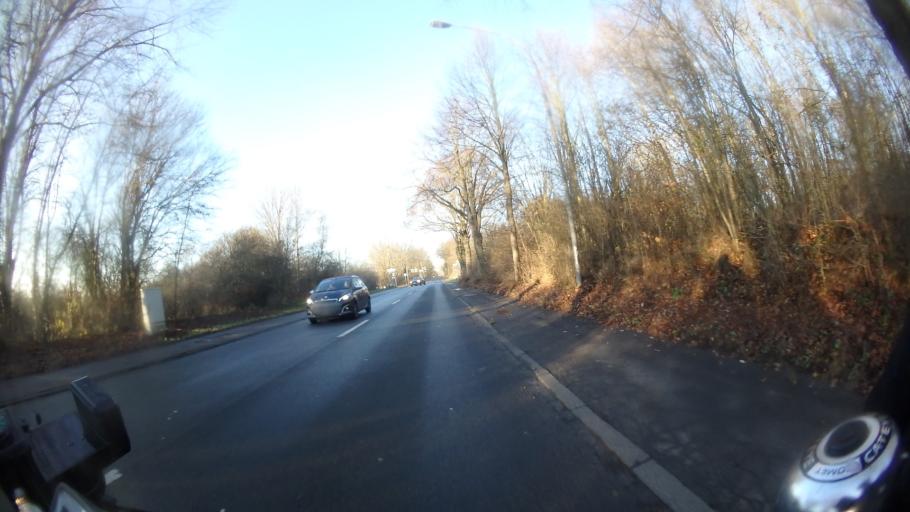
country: DE
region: Schleswig-Holstein
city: Travemuende
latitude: 53.9734
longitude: 10.8678
